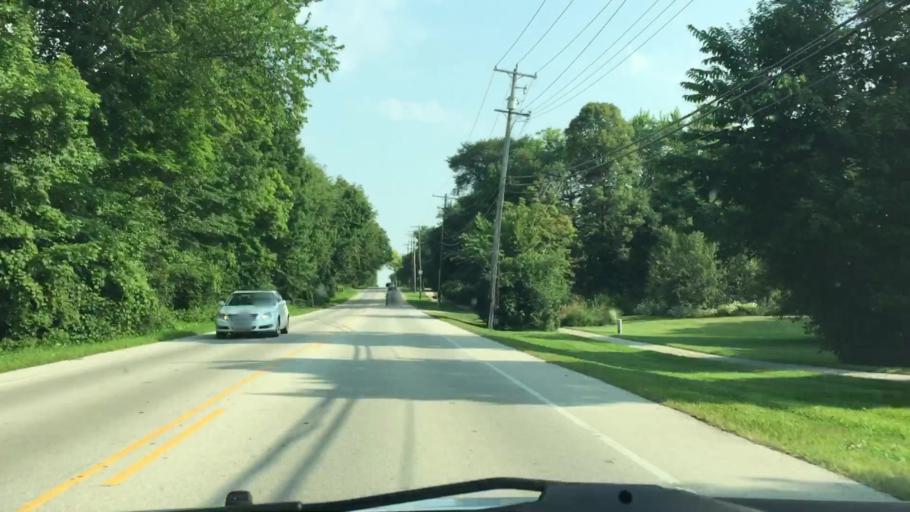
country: US
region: Wisconsin
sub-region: Waukesha County
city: Brookfield
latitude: 43.0569
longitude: -88.1461
